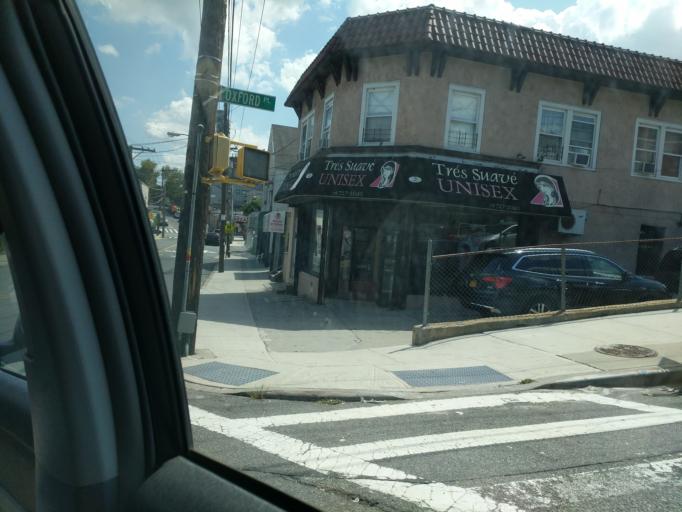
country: US
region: New Jersey
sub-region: Hudson County
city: Bayonne
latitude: 40.6345
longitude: -74.0868
